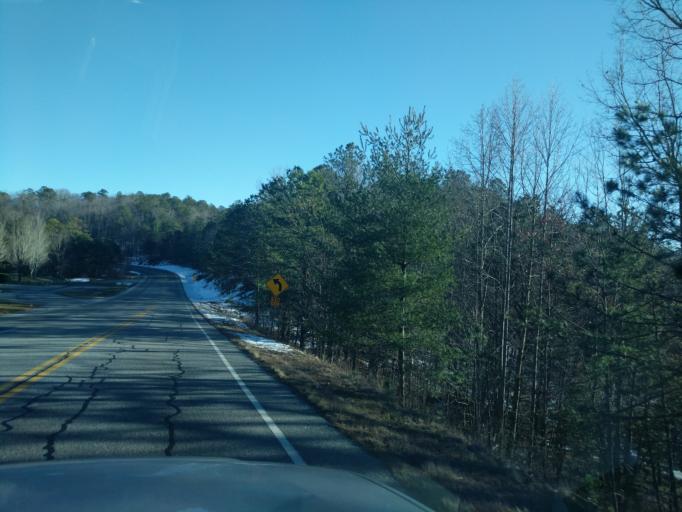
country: US
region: Georgia
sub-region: Rabun County
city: Clayton
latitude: 34.8758
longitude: -83.5761
